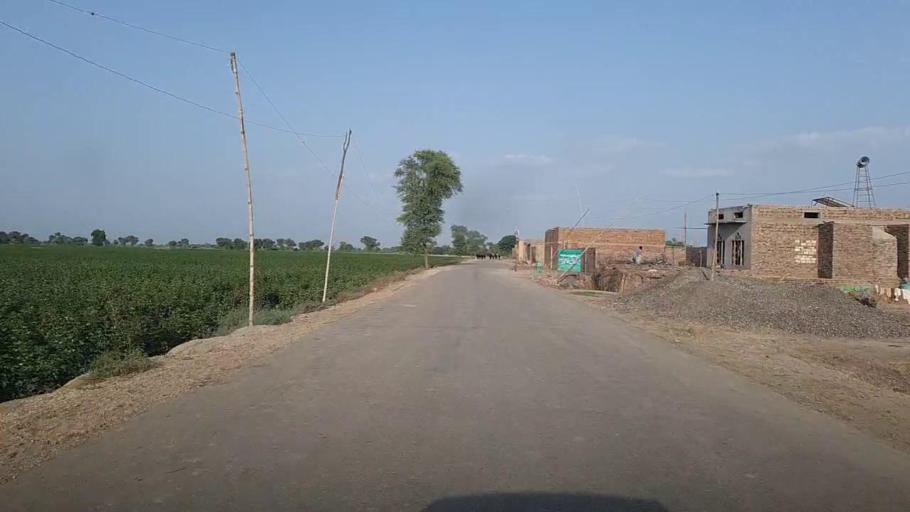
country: PK
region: Sindh
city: Khairpur
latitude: 28.0829
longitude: 69.7931
